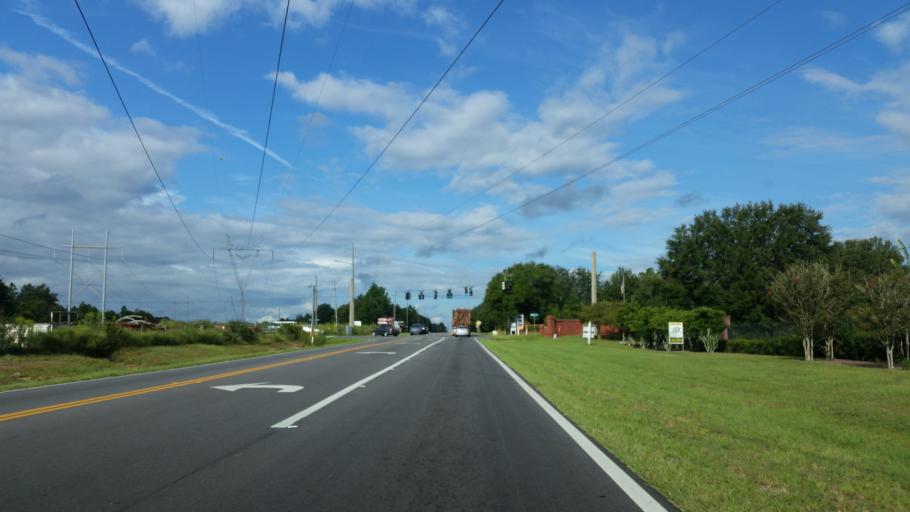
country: US
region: Florida
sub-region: Santa Rosa County
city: Wallace
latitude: 30.6474
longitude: -87.1464
